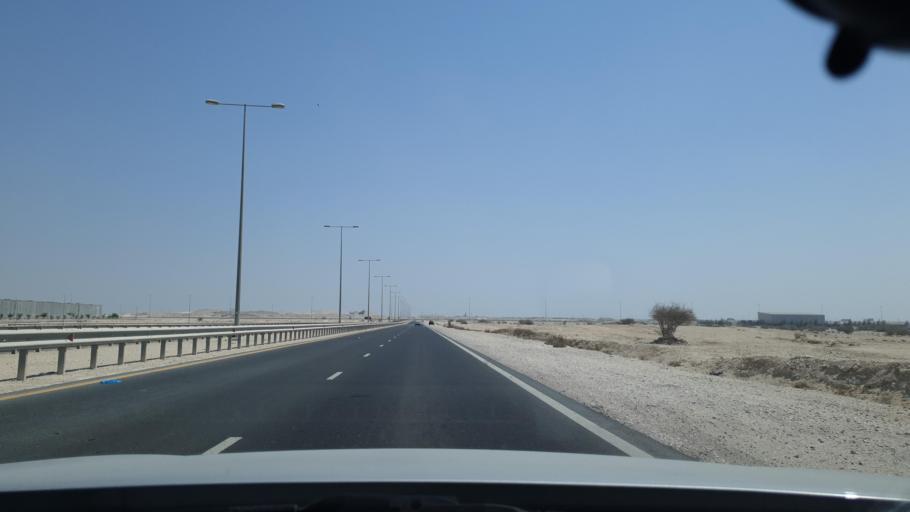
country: QA
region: Baladiyat Umm Salal
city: Umm Salal Muhammad
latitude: 25.3871
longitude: 51.3526
